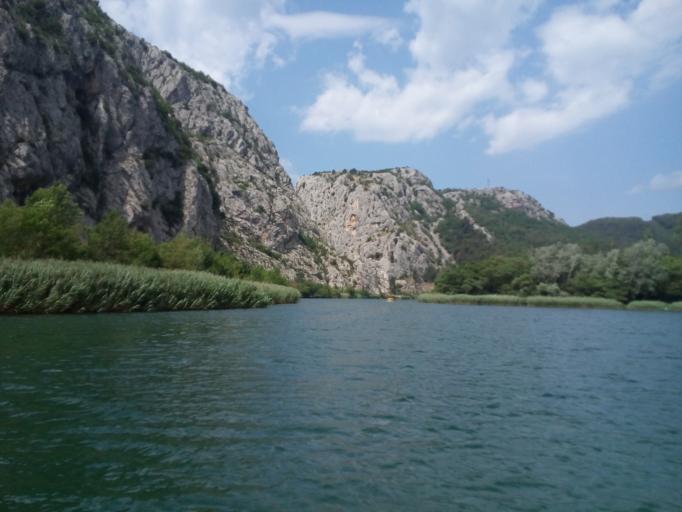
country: HR
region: Splitsko-Dalmatinska
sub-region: Grad Omis
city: Omis
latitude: 43.4511
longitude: 16.7034
